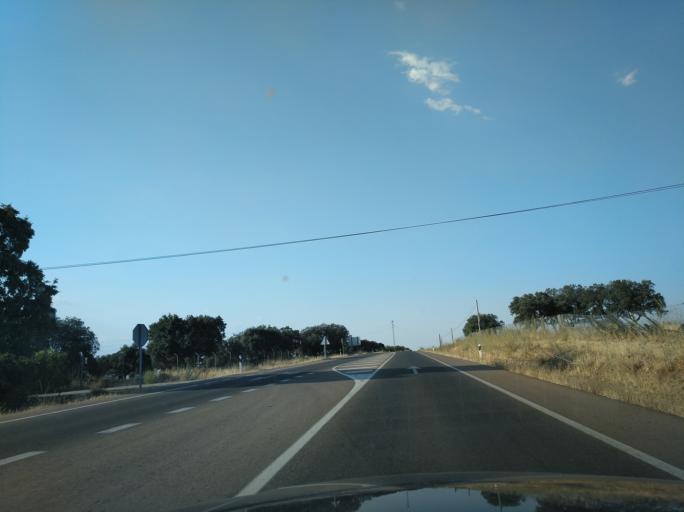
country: ES
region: Extremadura
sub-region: Provincia de Badajoz
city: Olivenza
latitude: 38.7114
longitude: -7.0857
